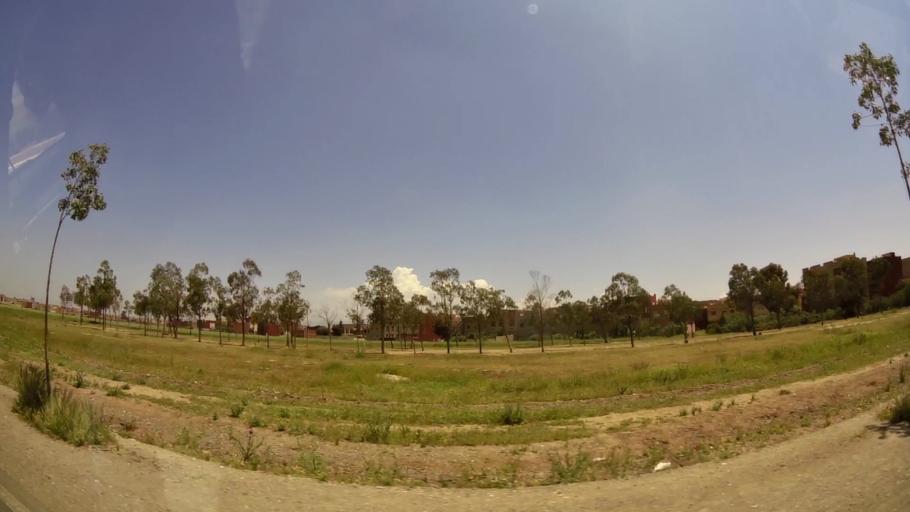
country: MA
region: Oriental
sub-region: Oujda-Angad
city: Oujda
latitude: 34.6654
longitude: -1.9523
